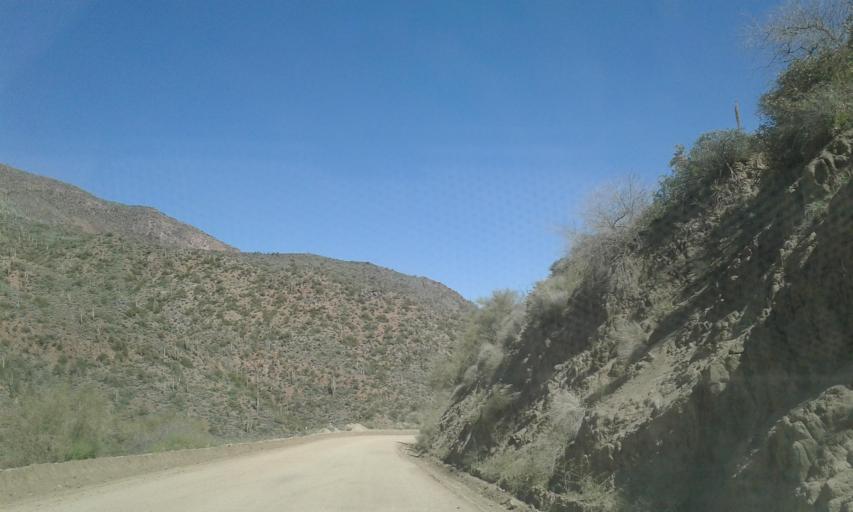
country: US
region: Arizona
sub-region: Gila County
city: Tonto Basin
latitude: 33.6579
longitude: -111.1806
